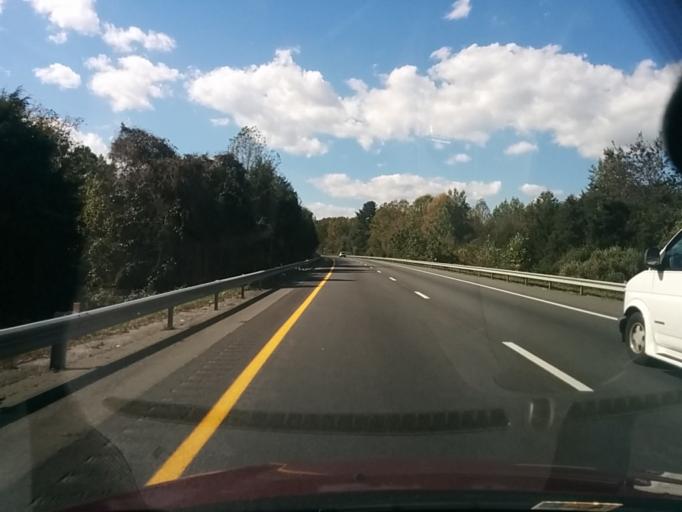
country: US
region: Virginia
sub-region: Albemarle County
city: Crozet
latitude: 38.0358
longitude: -78.6106
